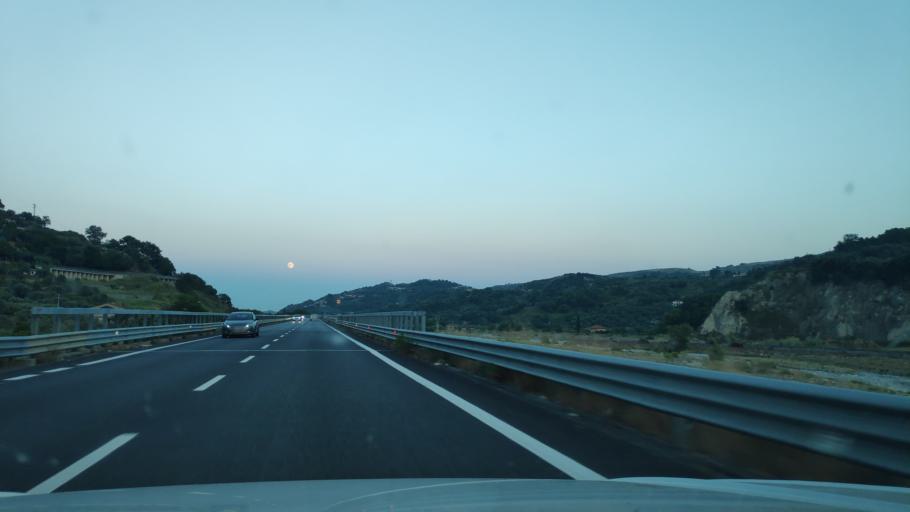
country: IT
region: Calabria
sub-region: Provincia di Reggio Calabria
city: Mammola
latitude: 38.3535
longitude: 16.2450
